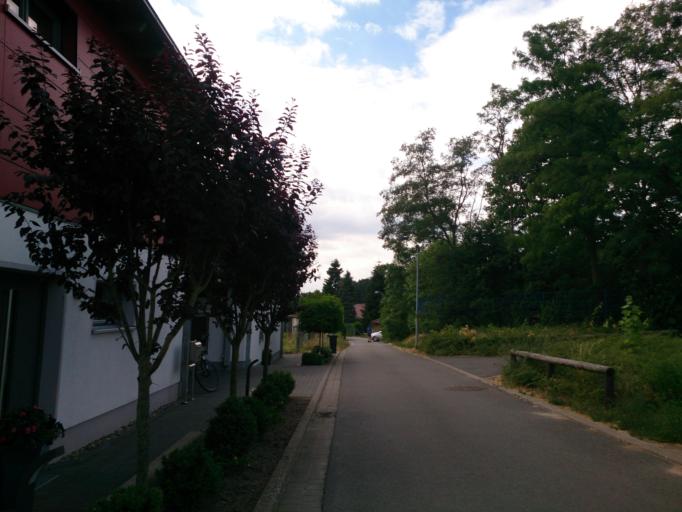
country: DE
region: Mecklenburg-Vorpommern
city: Waren
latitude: 53.5038
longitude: 12.6997
